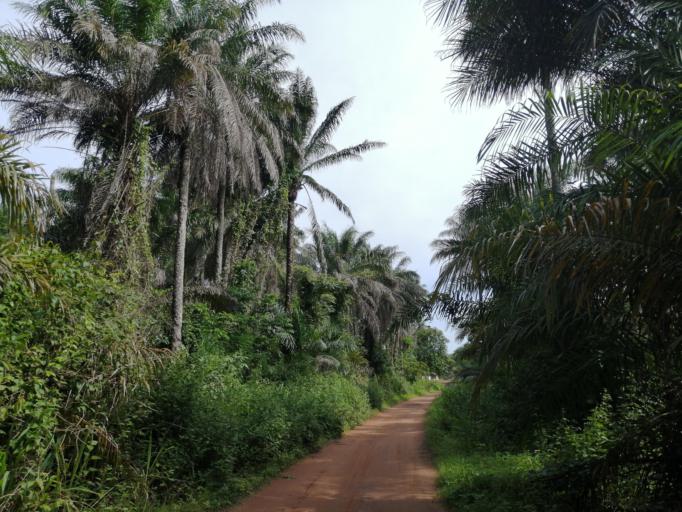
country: SL
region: Northern Province
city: Port Loko
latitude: 8.7855
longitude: -12.9243
